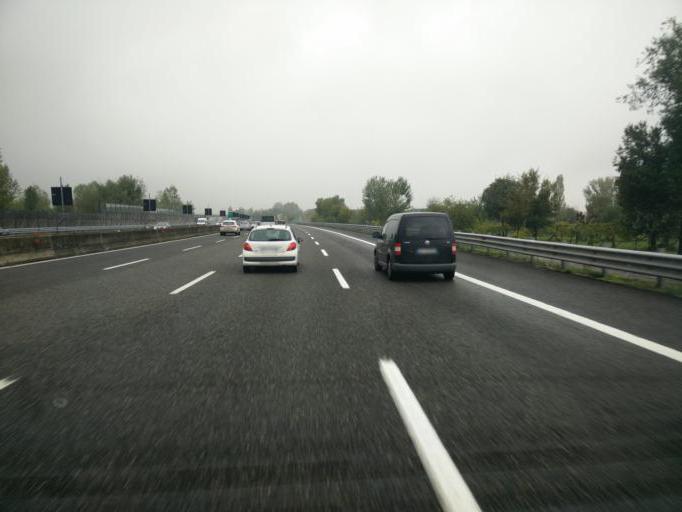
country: IT
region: Emilia-Romagna
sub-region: Provincia di Modena
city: San Cesario sul Panaro
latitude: 44.5642
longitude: 11.0458
